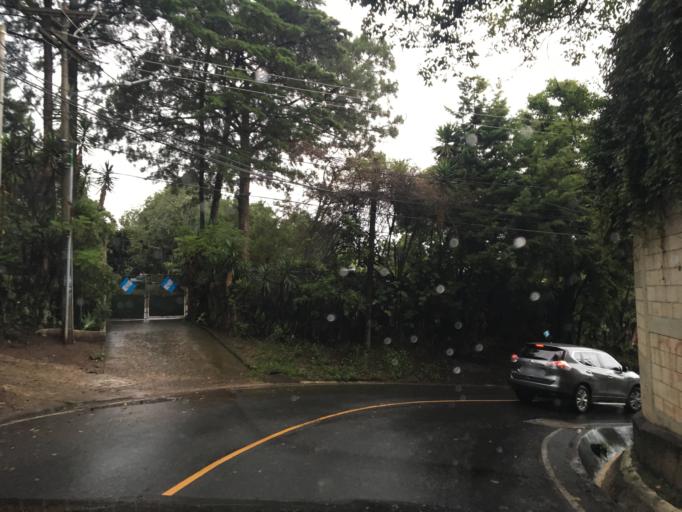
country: GT
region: Guatemala
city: Santa Catarina Pinula
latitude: 14.5563
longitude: -90.5038
